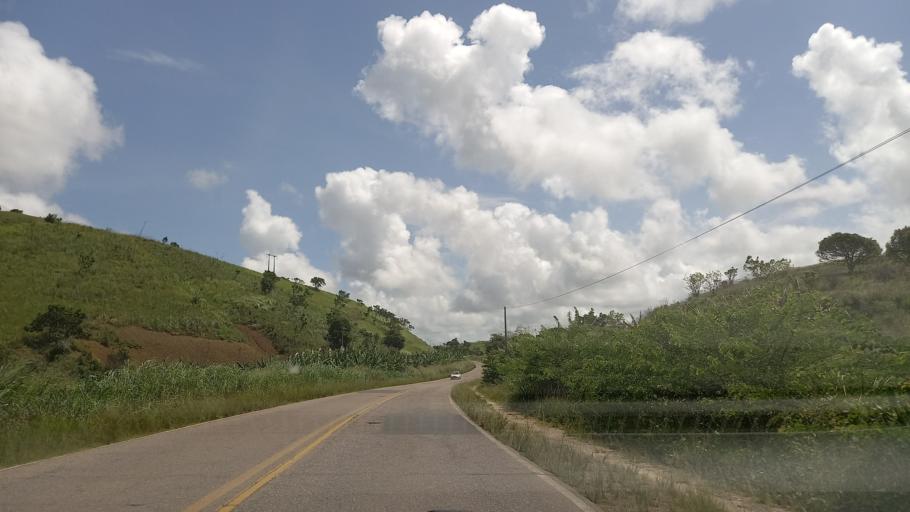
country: BR
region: Pernambuco
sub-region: Barreiros
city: Barreiros
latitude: -8.7840
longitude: -35.1805
